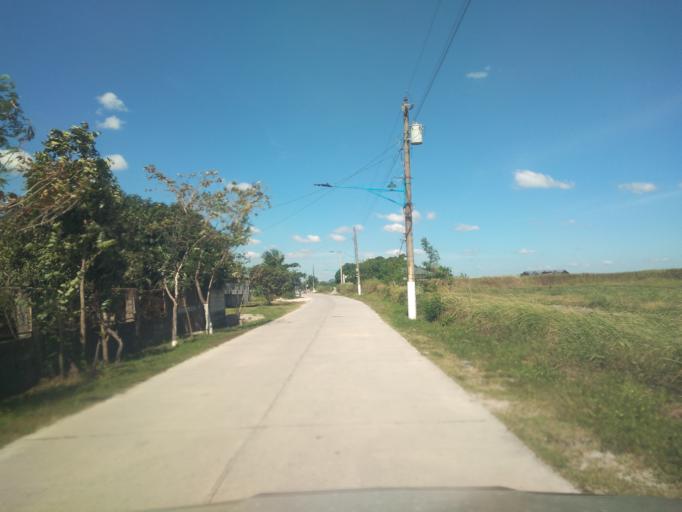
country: PH
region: Central Luzon
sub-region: Province of Pampanga
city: San Basilio
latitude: 15.0365
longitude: 120.6208
